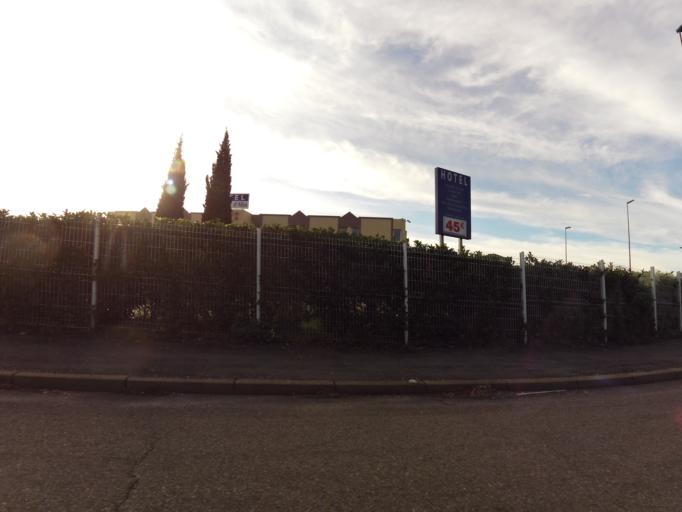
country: FR
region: Languedoc-Roussillon
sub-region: Departement du Gard
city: Ales
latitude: 44.1168
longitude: 4.1076
